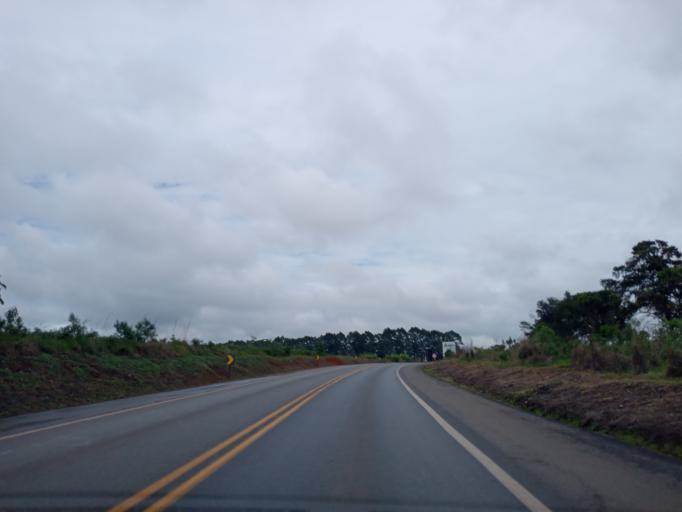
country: BR
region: Minas Gerais
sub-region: Campos Altos
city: Campos Altos
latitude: -19.6604
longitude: -46.2045
